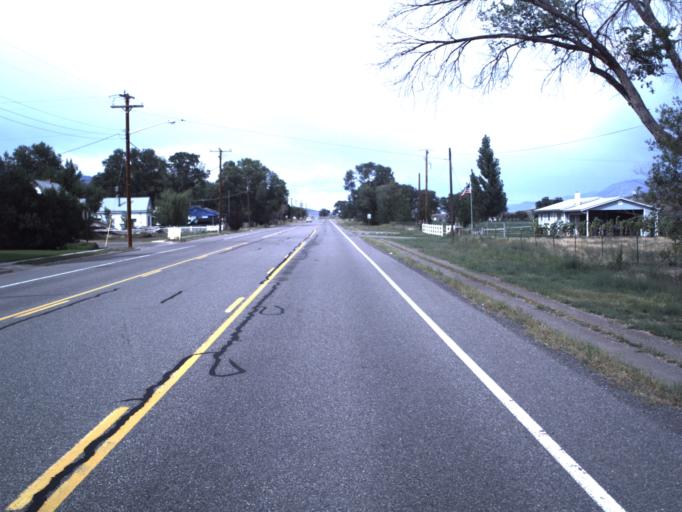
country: US
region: Utah
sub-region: Piute County
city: Junction
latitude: 38.2391
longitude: -112.2199
